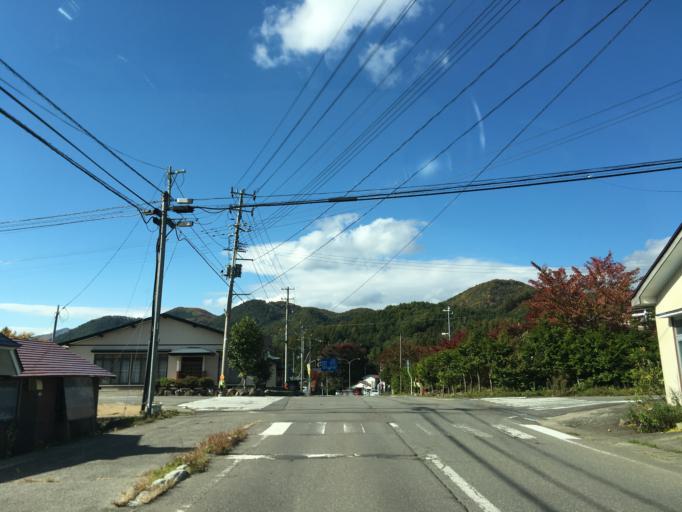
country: JP
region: Fukushima
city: Inawashiro
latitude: 37.6191
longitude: 140.2025
